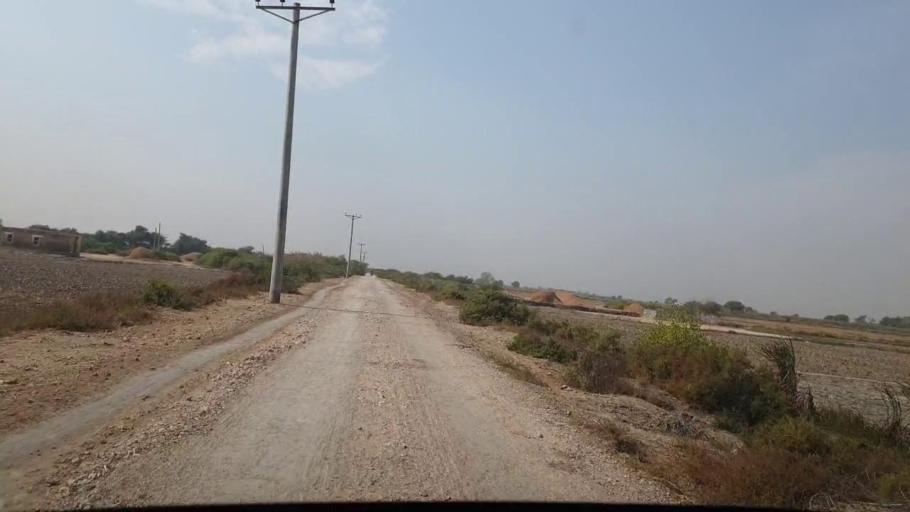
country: PK
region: Sindh
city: Chuhar Jamali
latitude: 24.2737
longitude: 67.9100
